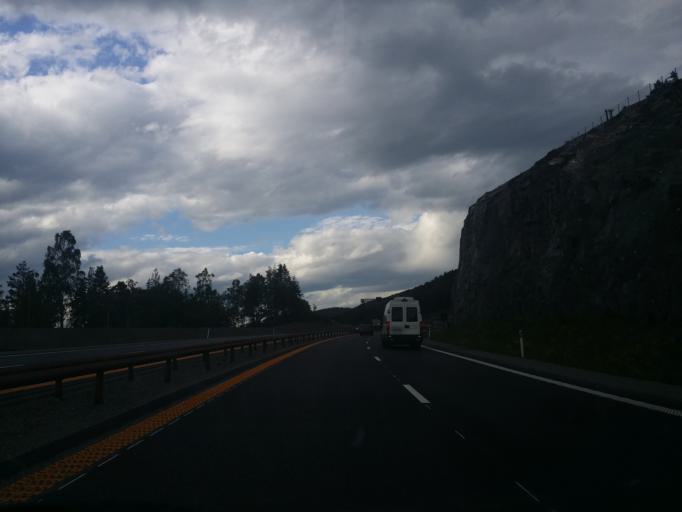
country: NO
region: Akershus
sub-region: Eidsvoll
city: Eidsvoll
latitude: 60.4571
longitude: 11.2397
